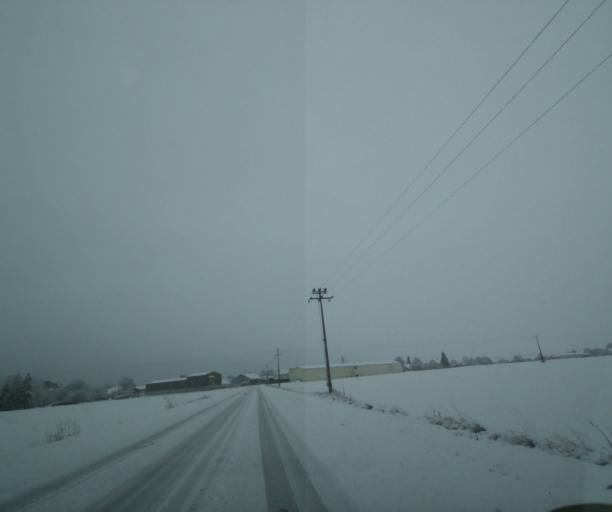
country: FR
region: Champagne-Ardenne
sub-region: Departement de la Haute-Marne
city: Saint-Dizier
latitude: 48.5834
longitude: 4.8925
